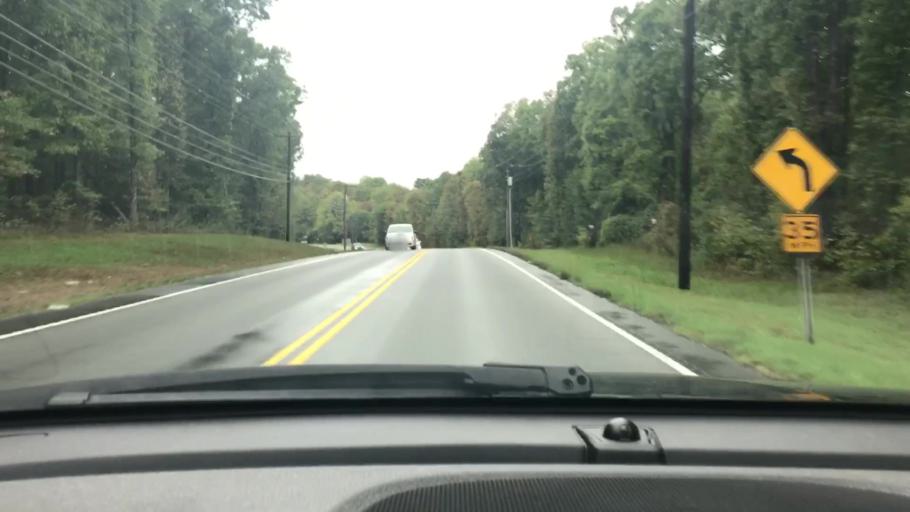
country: US
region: Tennessee
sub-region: Dickson County
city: White Bluff
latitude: 36.1090
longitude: -87.1700
